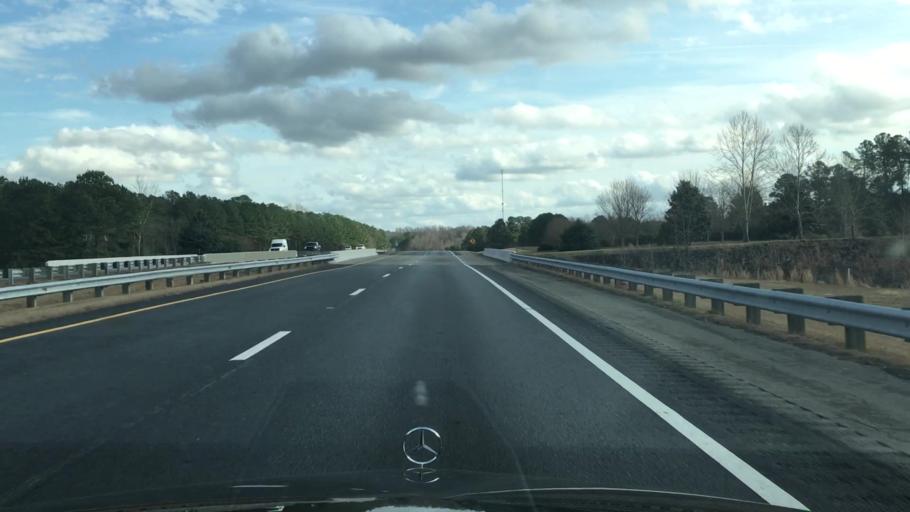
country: US
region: North Carolina
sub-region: Johnston County
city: Benson
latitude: 35.3297
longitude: -78.4497
